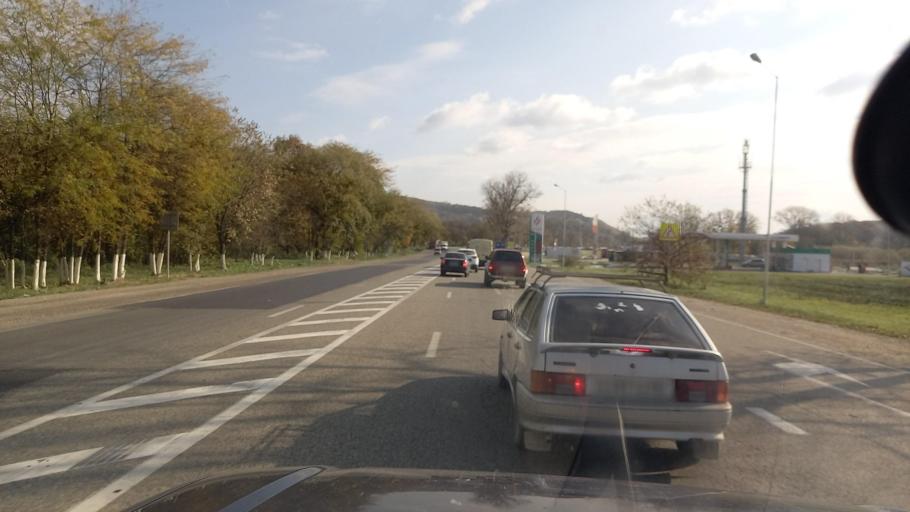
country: RU
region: Krasnodarskiy
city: Gayduk
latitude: 44.8726
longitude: 37.8259
